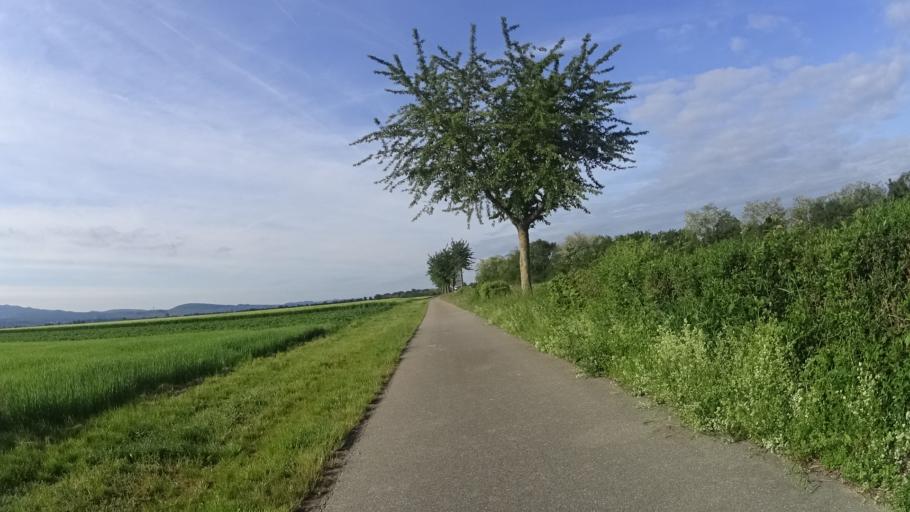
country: FR
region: Alsace
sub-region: Departement du Haut-Rhin
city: Blodelsheim
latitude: 47.8632
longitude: 7.5863
